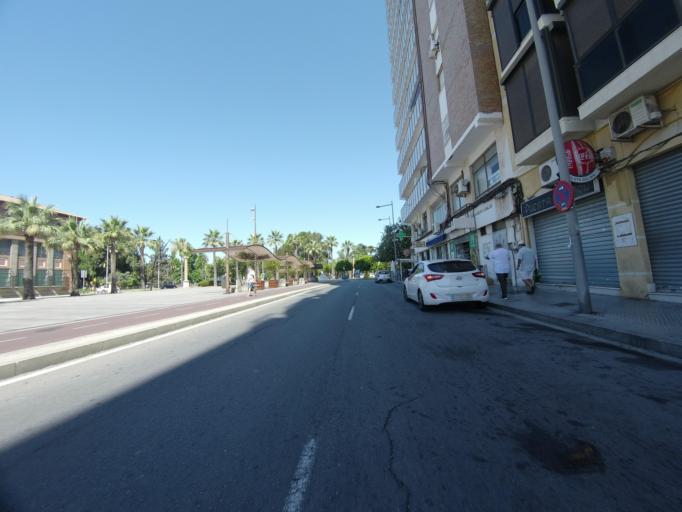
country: ES
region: Andalusia
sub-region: Provincia de Huelva
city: Huelva
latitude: 37.2556
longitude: -6.9564
